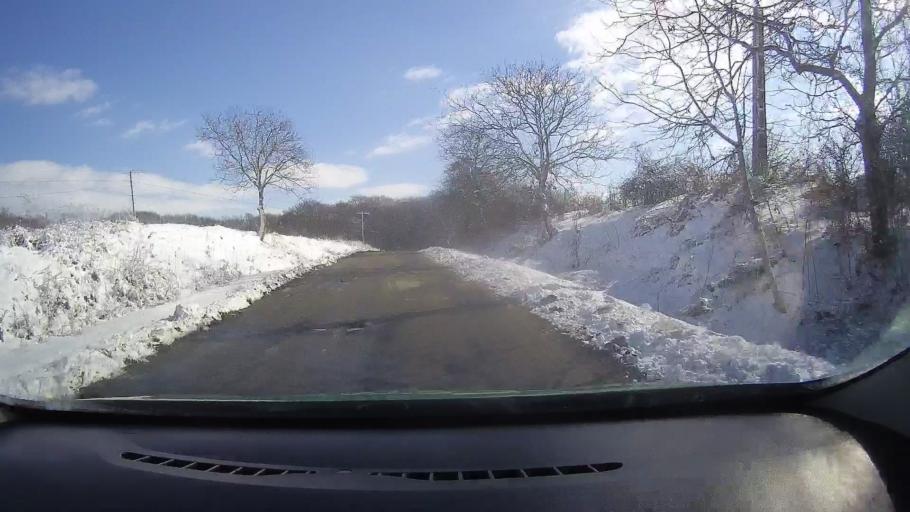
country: RO
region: Sibiu
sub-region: Comuna Mihaileni
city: Mihaileni
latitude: 46.0026
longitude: 24.4260
